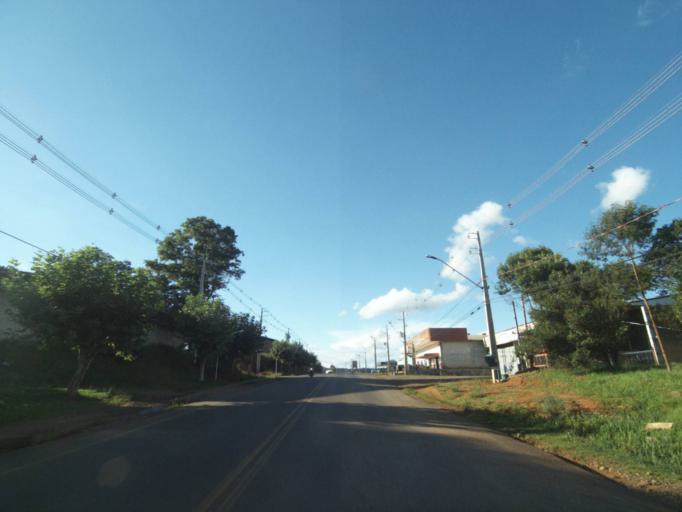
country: BR
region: Parana
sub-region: Uniao Da Vitoria
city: Uniao da Vitoria
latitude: -26.1650
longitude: -51.5361
